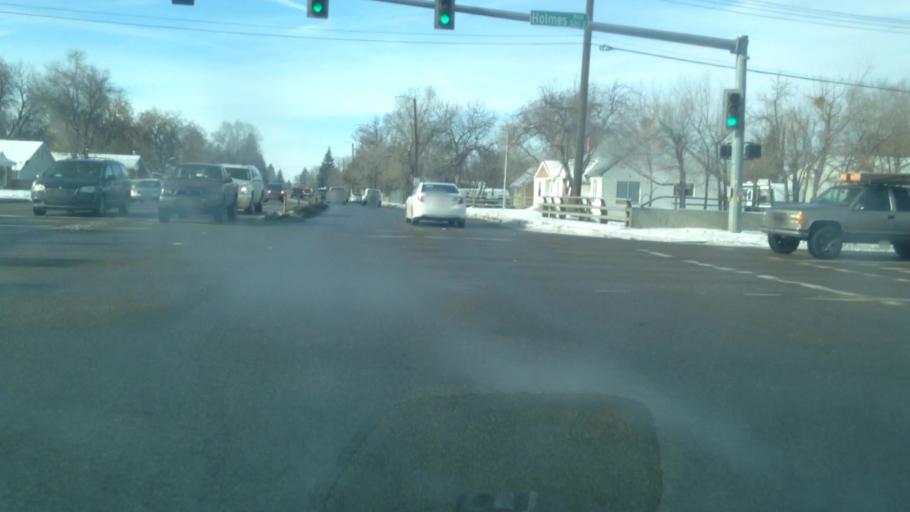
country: US
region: Idaho
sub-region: Bonneville County
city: Idaho Falls
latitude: 43.4826
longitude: -112.0236
